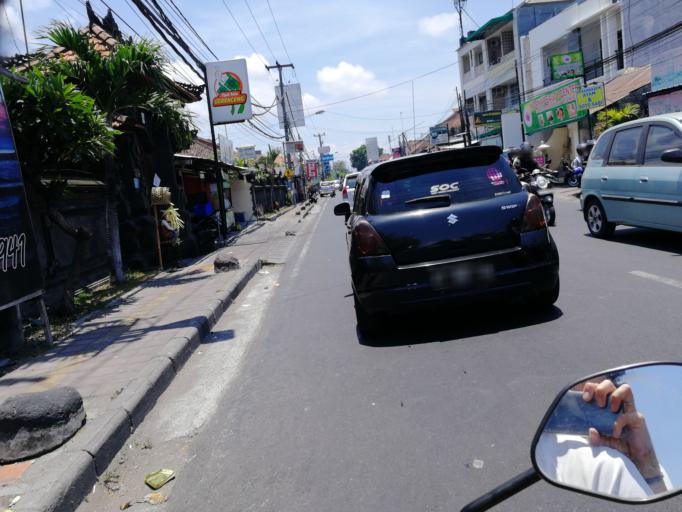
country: ID
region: Bali
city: Karyadharma
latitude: -8.6867
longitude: 115.1932
